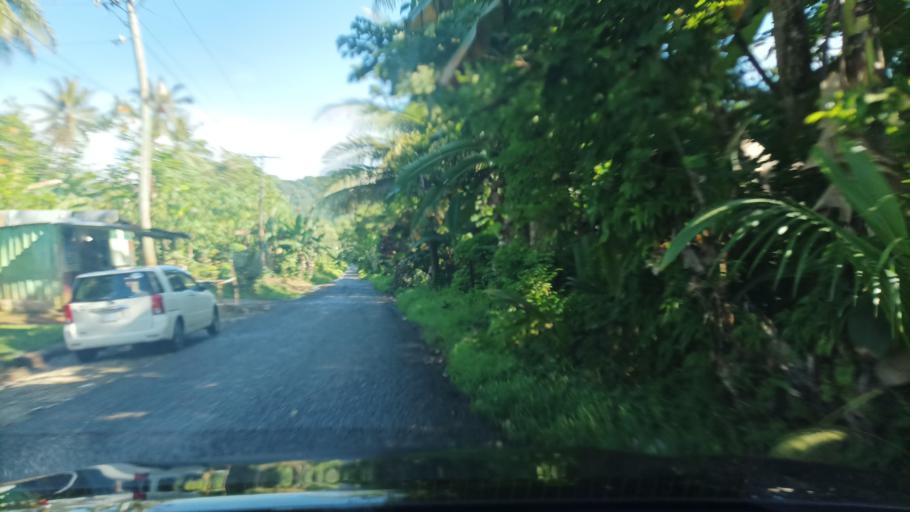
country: FM
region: Pohnpei
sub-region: Sokehs Municipality
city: Palikir - National Government Center
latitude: 6.9172
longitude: 158.1581
